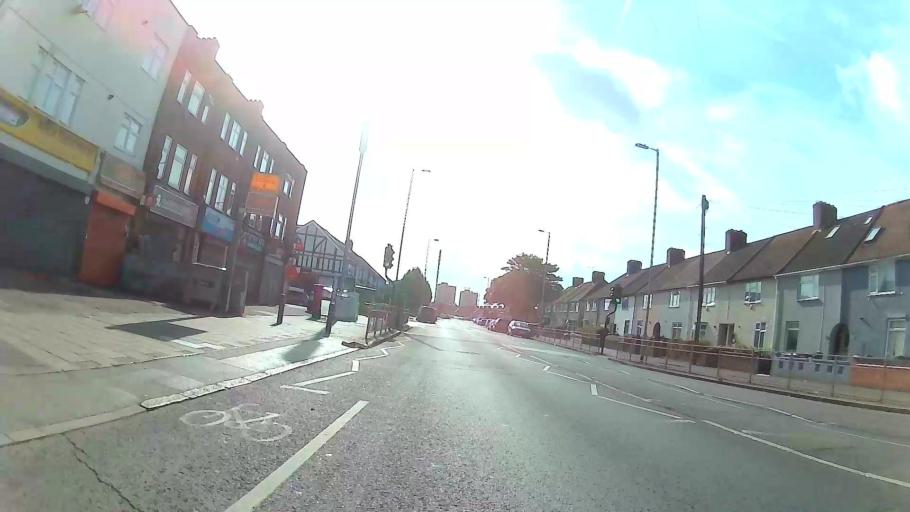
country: GB
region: England
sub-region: Greater London
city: Chadwell Heath
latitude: 51.5613
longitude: 0.1400
